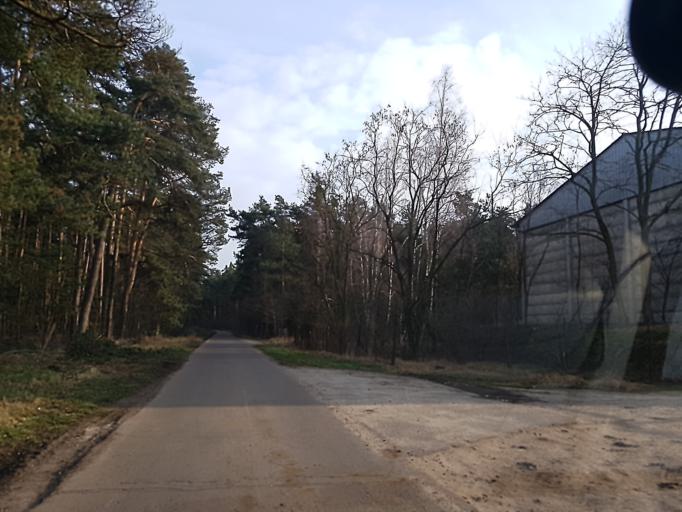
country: DE
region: Brandenburg
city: Wollin
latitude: 52.2737
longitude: 12.4847
